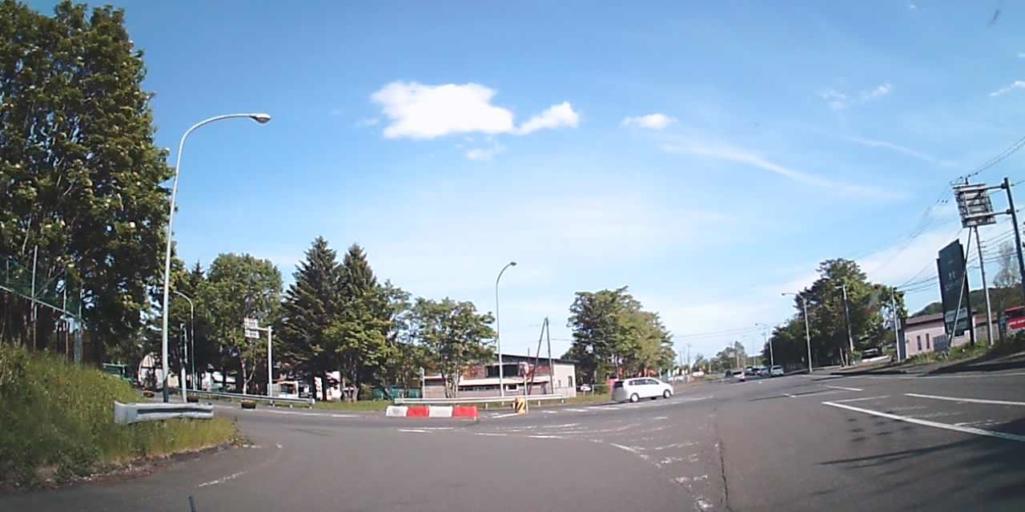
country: JP
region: Hokkaido
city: Tomakomai
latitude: 42.6303
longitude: 141.4878
